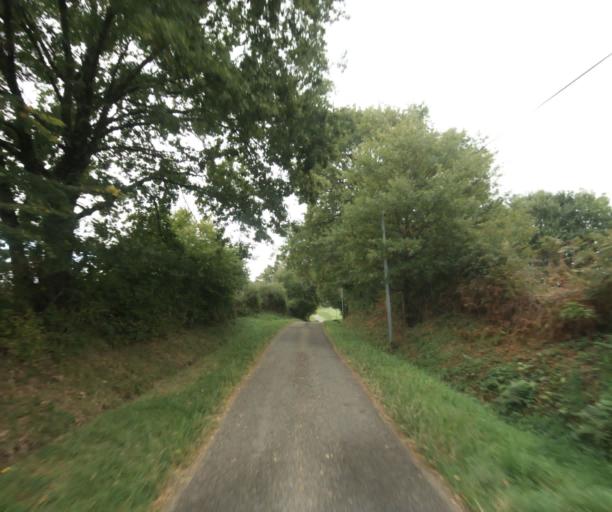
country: FR
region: Midi-Pyrenees
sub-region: Departement du Gers
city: Eauze
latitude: 43.8988
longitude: 0.0527
